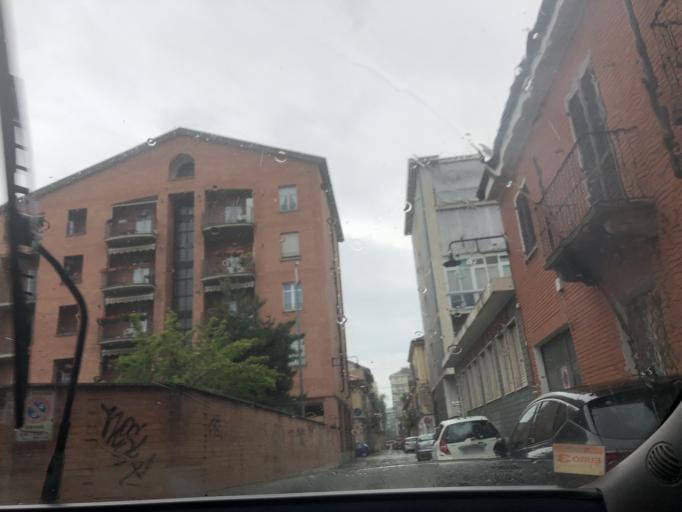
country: IT
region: Piedmont
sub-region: Provincia di Torino
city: Turin
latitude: 45.0800
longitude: 7.6524
